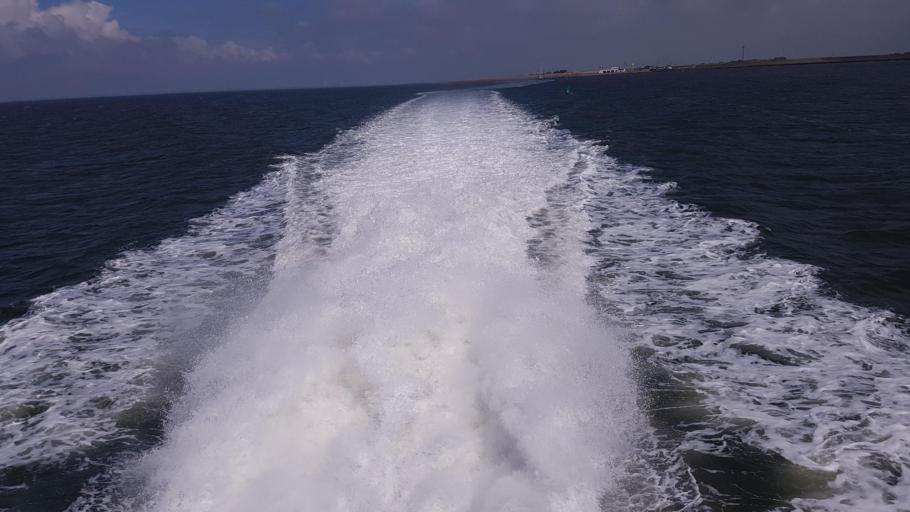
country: DE
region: Schleswig-Holstein
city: Elisabeth-Sophien-Koog
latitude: 54.4940
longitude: 8.7908
